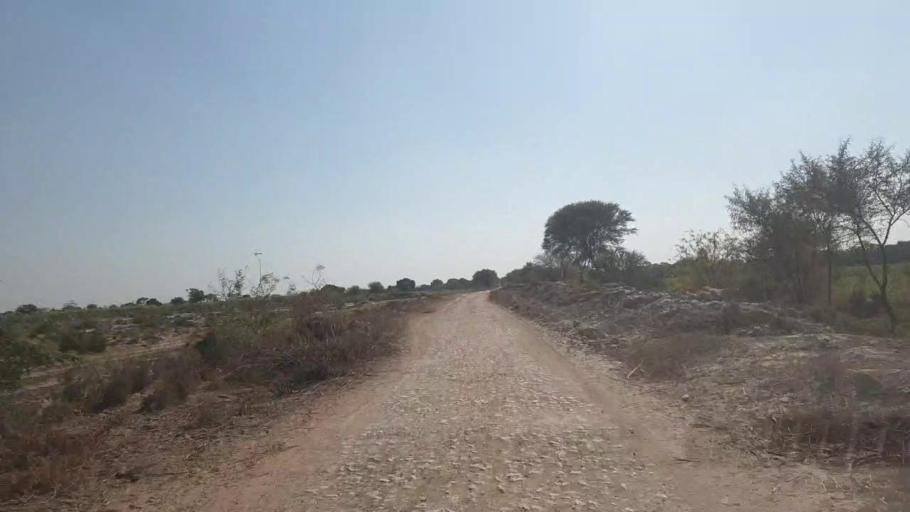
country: PK
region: Sindh
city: Chambar
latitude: 25.3158
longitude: 68.7409
